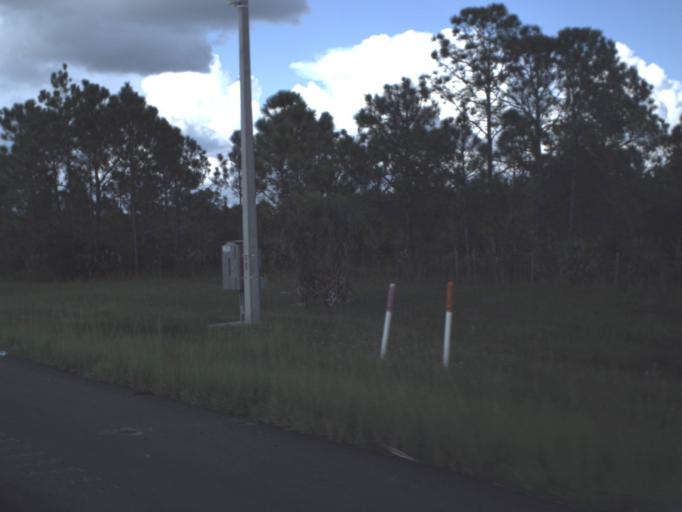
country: US
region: Florida
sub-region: Charlotte County
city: Charlotte Park
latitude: 26.8464
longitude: -81.9685
